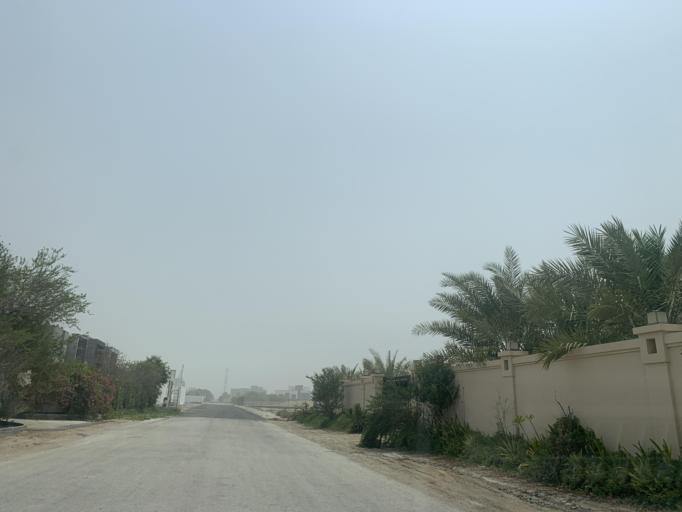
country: BH
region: Central Governorate
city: Madinat Hamad
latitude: 26.1676
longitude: 50.4740
